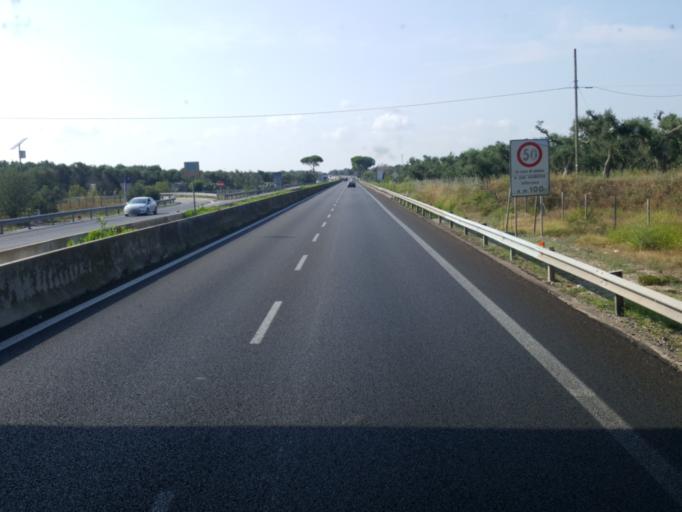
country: IT
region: Apulia
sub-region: Provincia di Lecce
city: Trepuzzi
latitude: 40.4396
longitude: 18.0784
